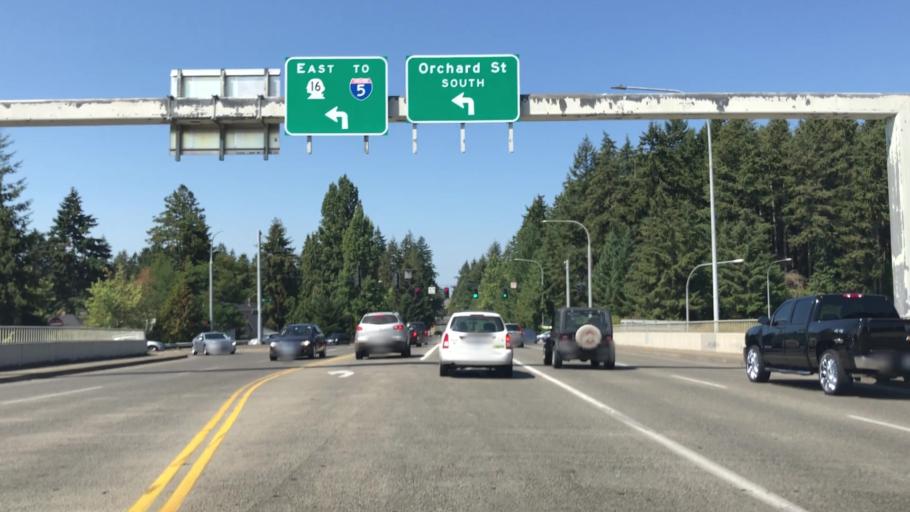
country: US
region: Washington
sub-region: Pierce County
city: Fircrest
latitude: 47.2429
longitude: -122.5042
